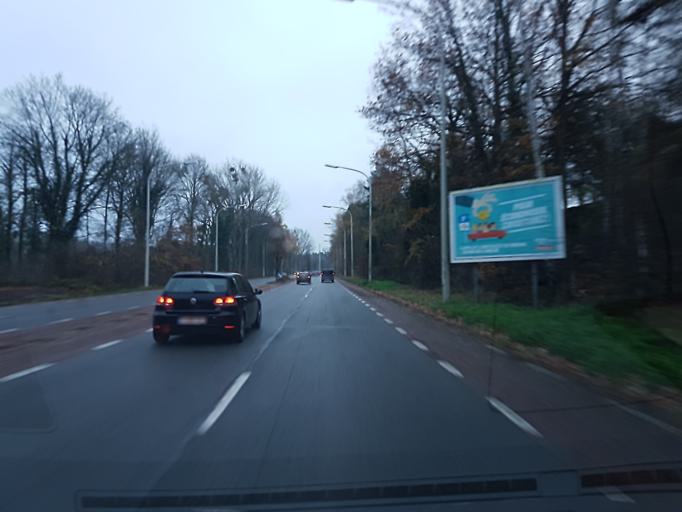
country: BE
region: Wallonia
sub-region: Province de Namur
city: Namur
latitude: 50.4578
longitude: 4.8916
